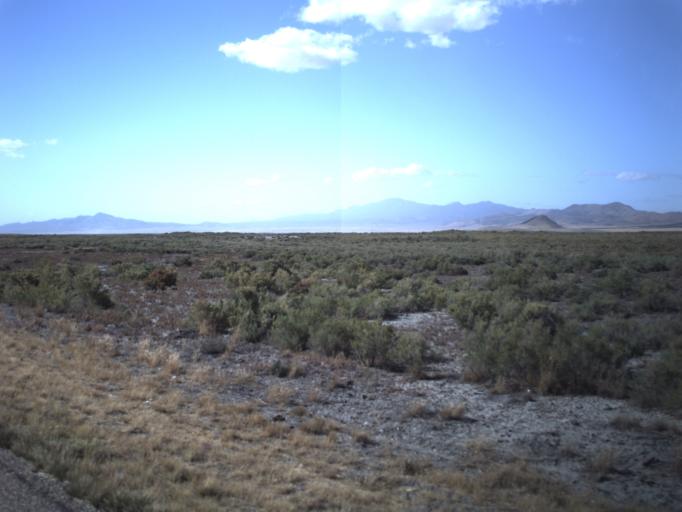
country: US
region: Utah
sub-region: Beaver County
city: Milford
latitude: 38.7272
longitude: -112.9671
